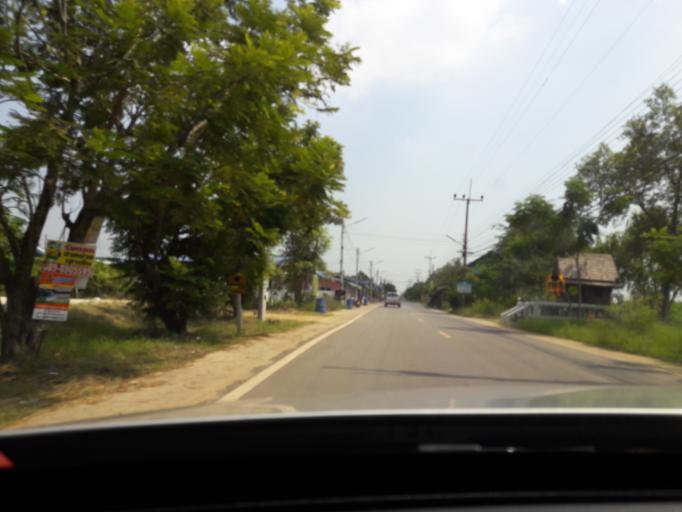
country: TH
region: Samut Songkhram
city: Amphawa
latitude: 13.3506
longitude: 99.9363
